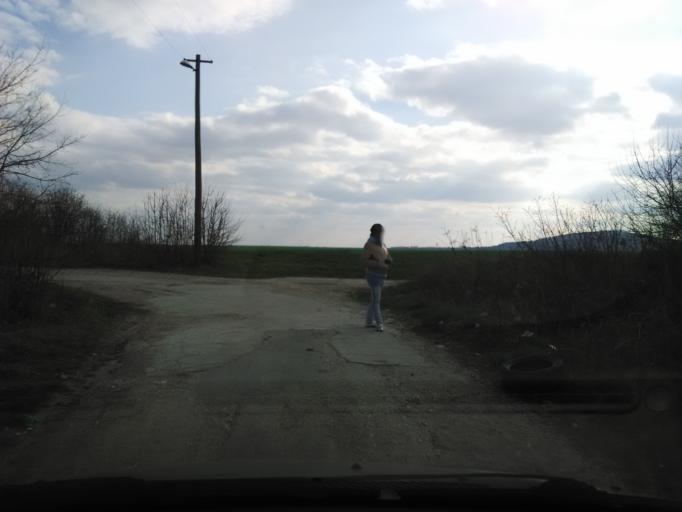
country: SK
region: Nitriansky
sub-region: Okres Nitra
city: Vrable
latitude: 48.3695
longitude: 18.2293
